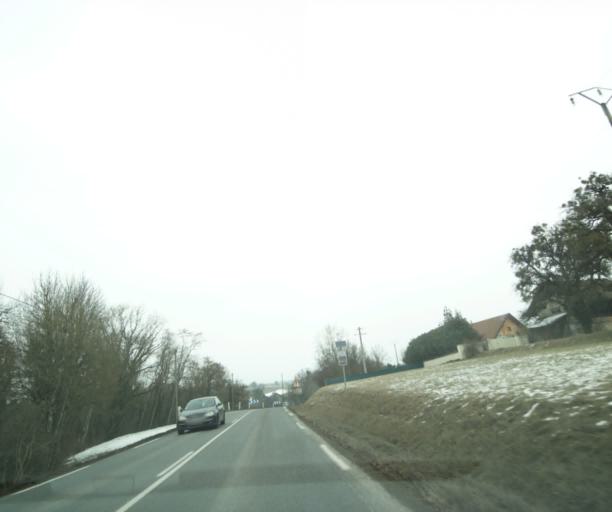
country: FR
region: Rhone-Alpes
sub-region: Departement de la Haute-Savoie
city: Contamine-sur-Arve
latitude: 46.1317
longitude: 6.3127
